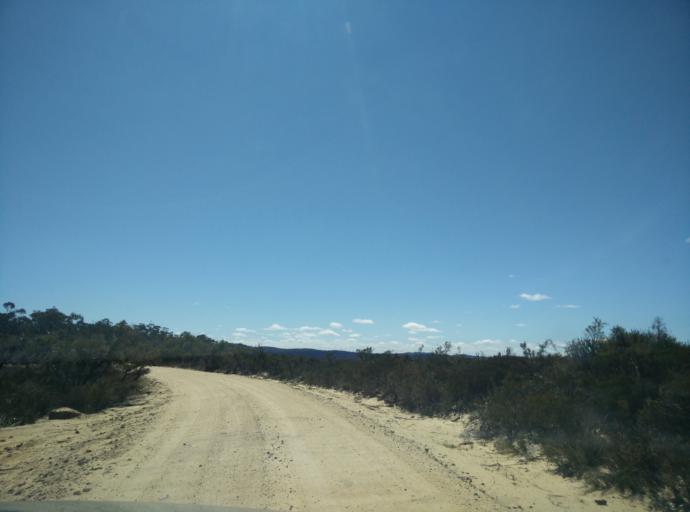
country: AU
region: New South Wales
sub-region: Blue Mountains Municipality
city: Blackheath
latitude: -33.5721
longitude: 150.2783
